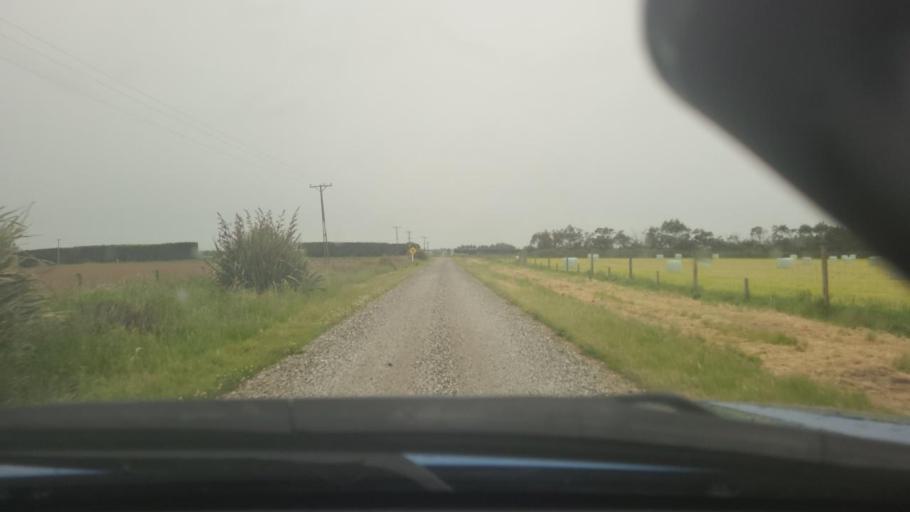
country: NZ
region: Southland
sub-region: Invercargill City
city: Invercargill
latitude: -46.4426
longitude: 168.4847
